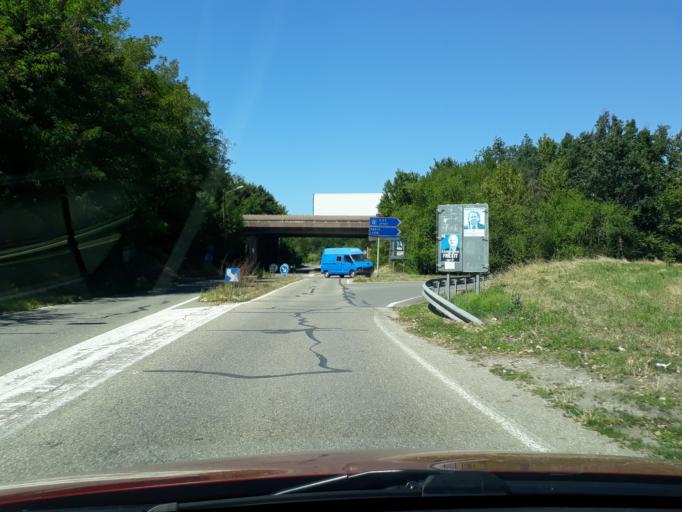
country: FR
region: Rhone-Alpes
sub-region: Departement du Rhone
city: Saint-Priest
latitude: 45.6914
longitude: 4.9687
